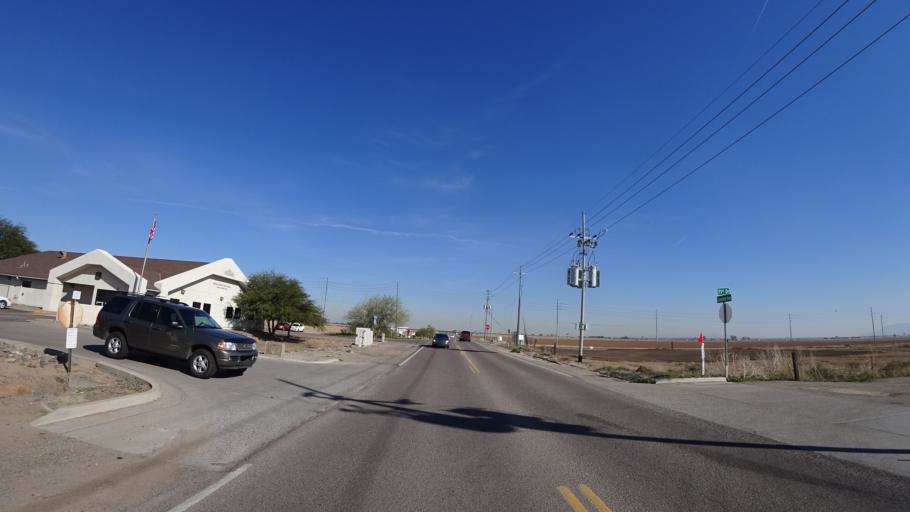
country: US
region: Arizona
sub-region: Maricopa County
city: Citrus Park
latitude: 33.5373
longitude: -112.4276
